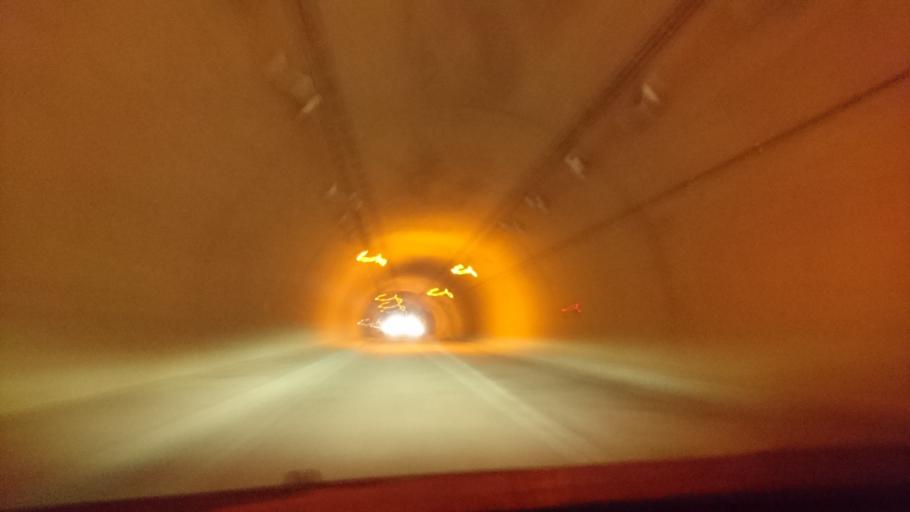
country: JP
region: Miyagi
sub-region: Oshika Gun
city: Onagawa Cho
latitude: 38.5864
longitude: 141.4786
